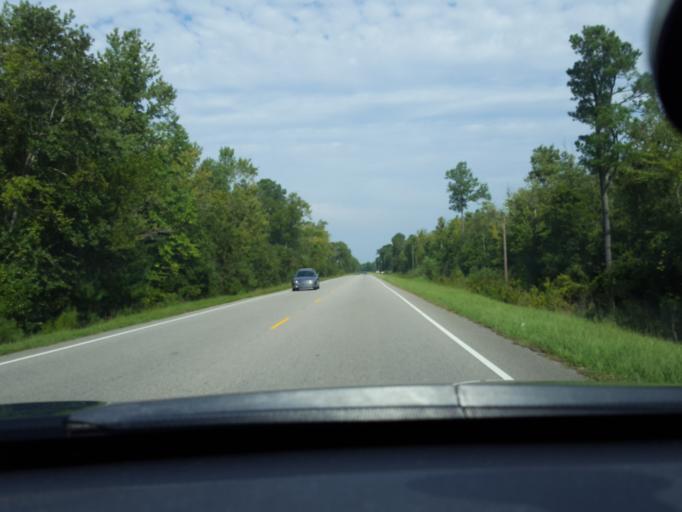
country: US
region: North Carolina
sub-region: Washington County
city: Plymouth
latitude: 35.8990
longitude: -76.7084
